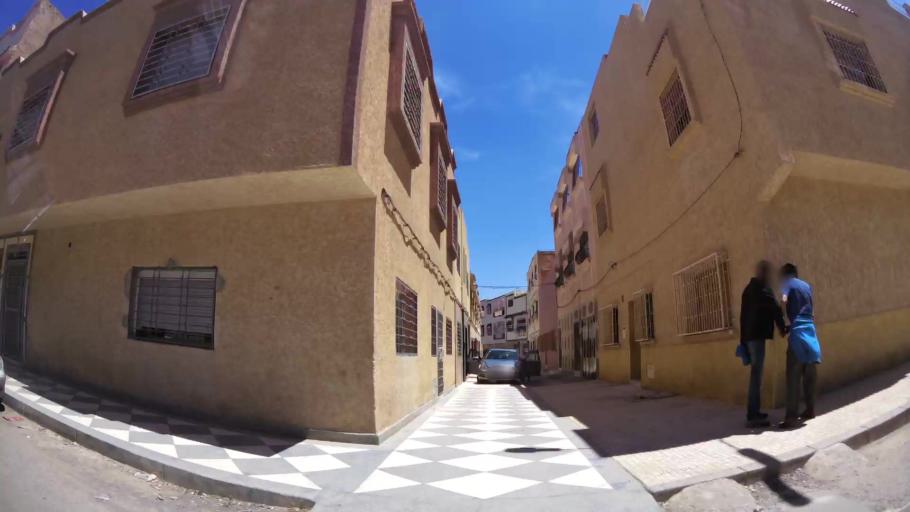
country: MA
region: Oriental
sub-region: Oujda-Angad
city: Oujda
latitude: 34.6652
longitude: -1.9352
